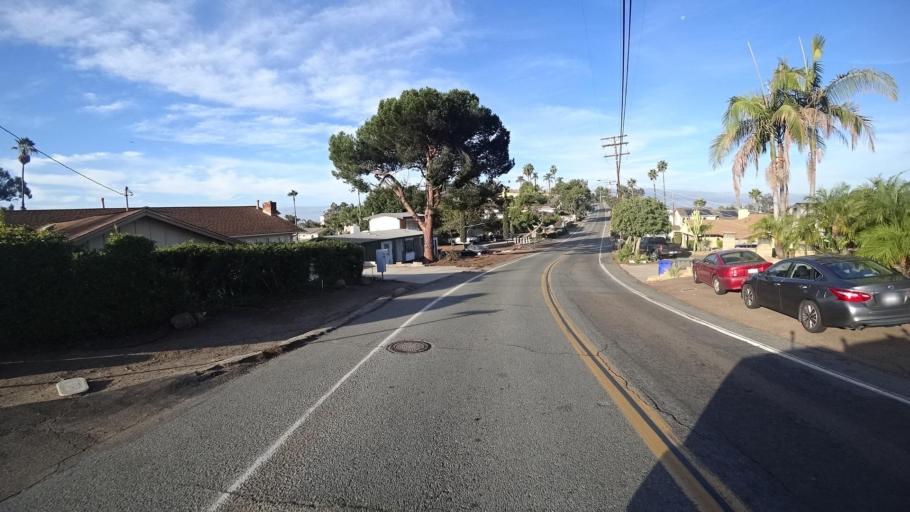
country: US
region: California
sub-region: San Diego County
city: La Presa
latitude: 32.7246
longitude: -117.0037
